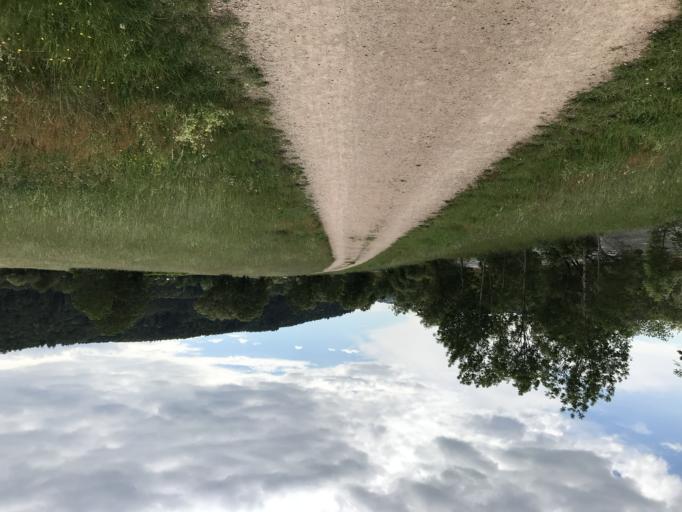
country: DE
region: Baden-Wuerttemberg
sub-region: Freiburg Region
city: Hausen
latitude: 47.6730
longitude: 7.8396
